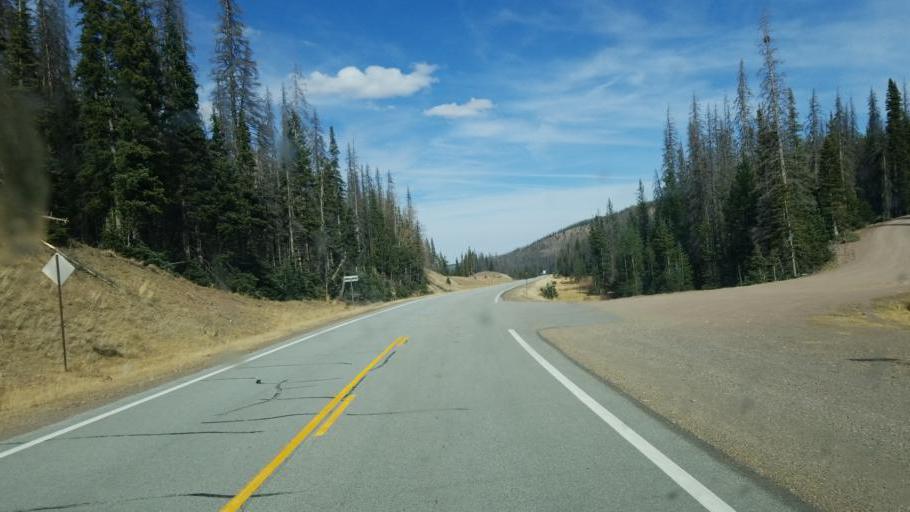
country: US
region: New Mexico
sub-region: Rio Arriba County
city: Chama
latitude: 37.0799
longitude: -106.3850
